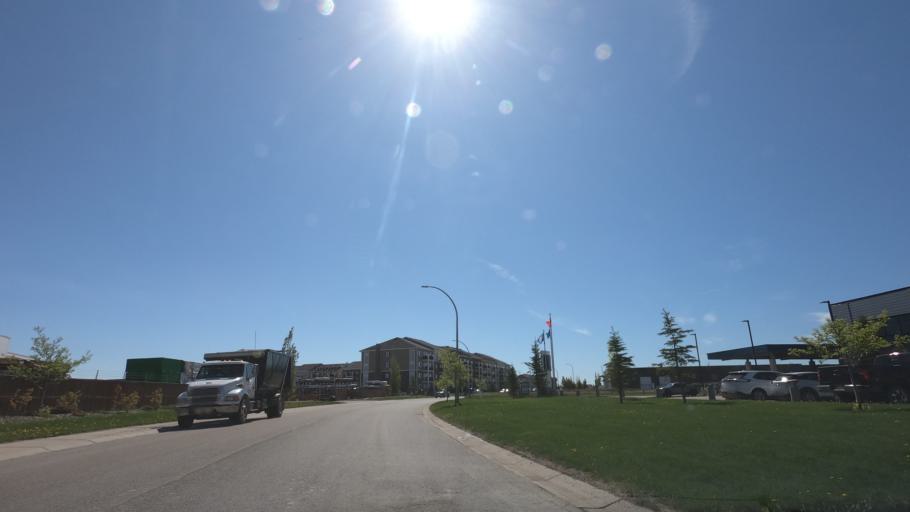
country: CA
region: Alberta
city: Airdrie
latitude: 51.2674
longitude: -113.9961
